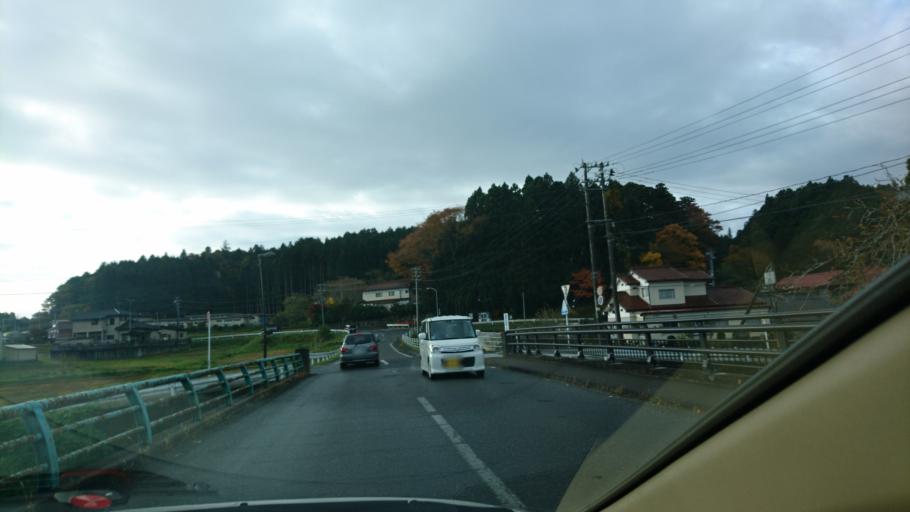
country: JP
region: Iwate
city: Ofunato
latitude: 38.9101
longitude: 141.5446
